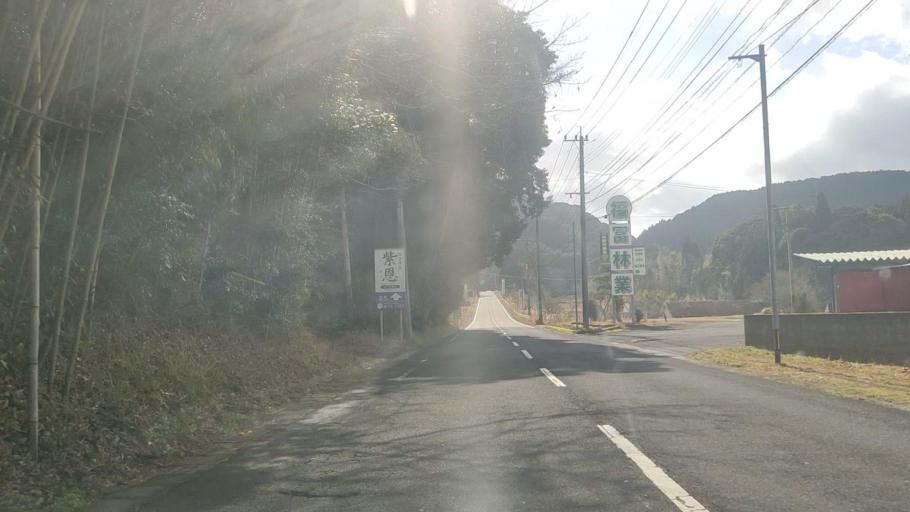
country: JP
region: Kagoshima
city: Okuchi-shinohara
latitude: 31.9813
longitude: 130.7425
